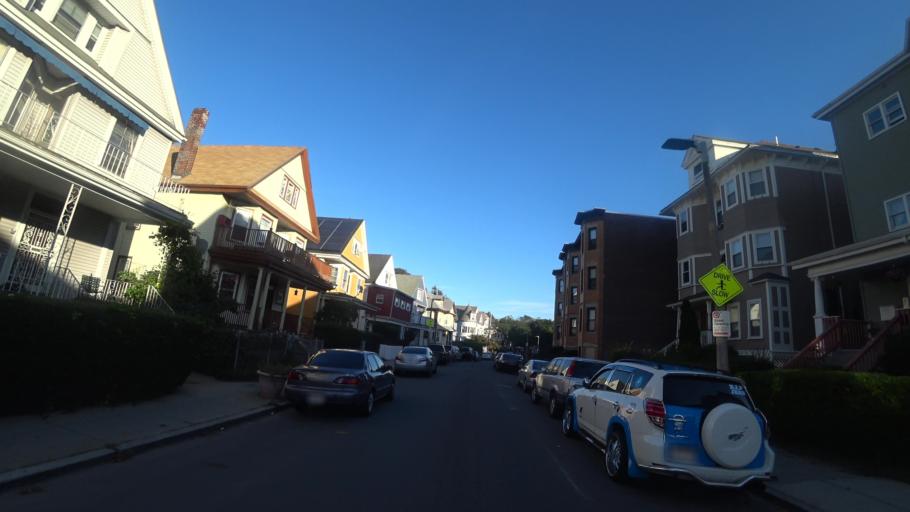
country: US
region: Massachusetts
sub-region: Suffolk County
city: South Boston
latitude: 42.3104
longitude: -71.0805
